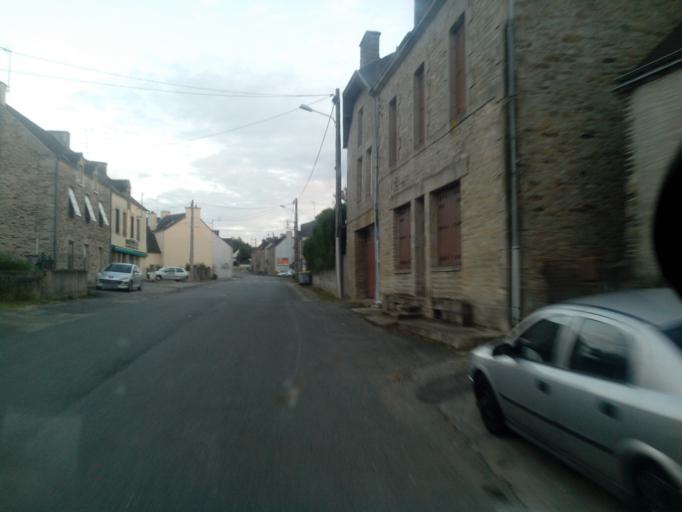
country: FR
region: Brittany
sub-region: Departement du Morbihan
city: Guegon
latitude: 47.9380
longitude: -2.5645
